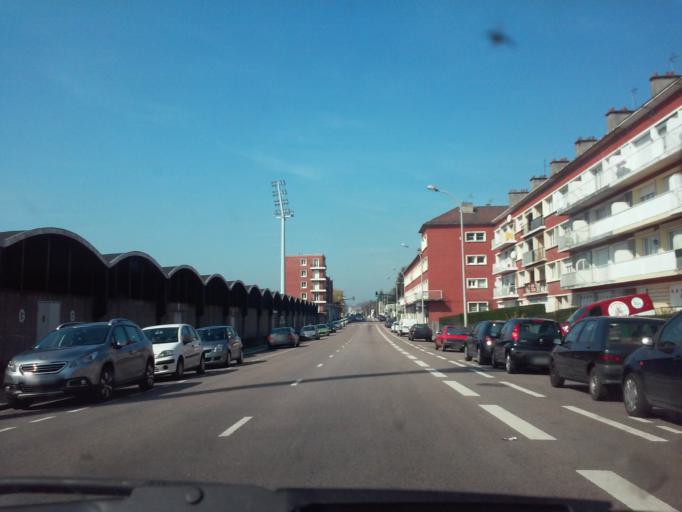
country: FR
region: Haute-Normandie
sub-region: Departement de la Seine-Maritime
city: Harfleur
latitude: 49.5025
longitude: 0.1723
